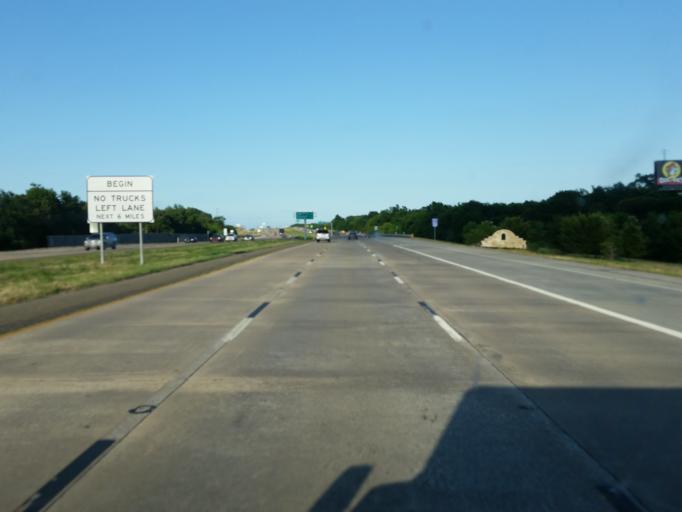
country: US
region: Texas
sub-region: Dallas County
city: Balch Springs
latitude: 32.7018
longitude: -96.6157
